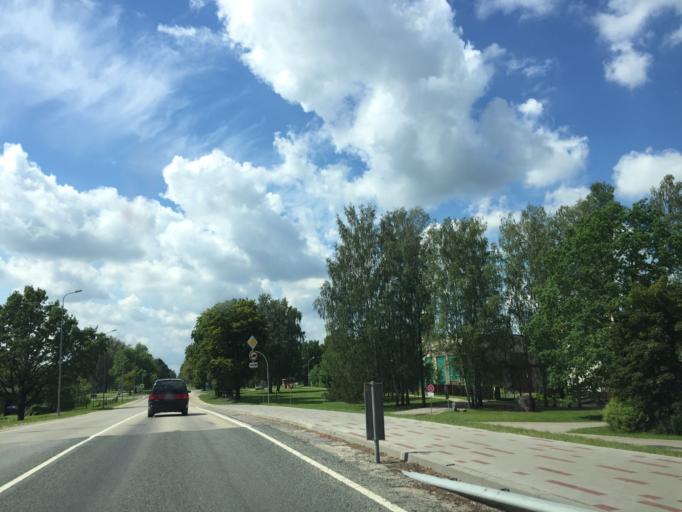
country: LV
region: Ozolnieku
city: Ozolnieki
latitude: 56.6919
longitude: 23.7975
